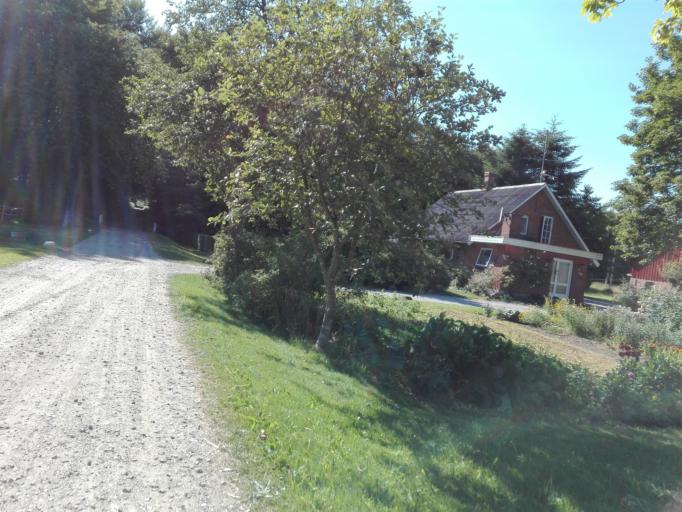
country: DK
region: Central Jutland
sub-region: Odder Kommune
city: Odder
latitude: 55.9579
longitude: 10.0848
